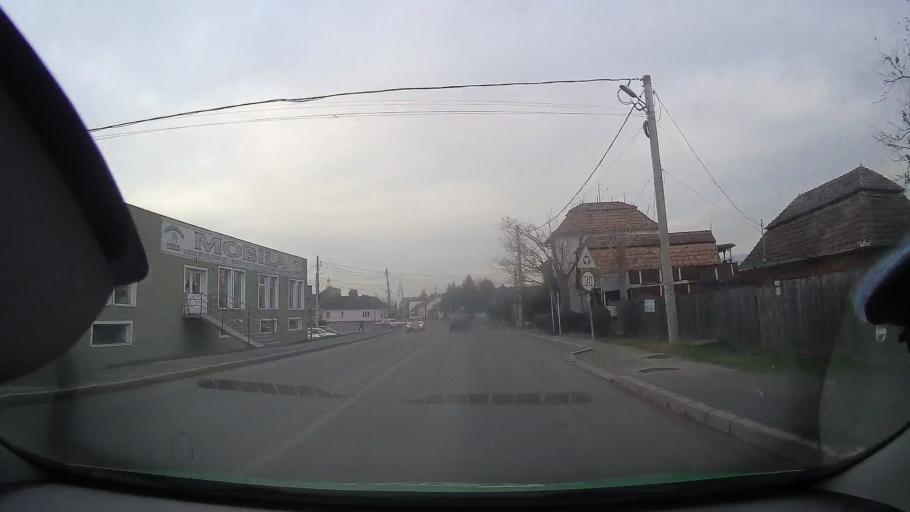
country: RO
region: Mures
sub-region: Comuna Ludus
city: Ludus
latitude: 46.4808
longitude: 24.0960
